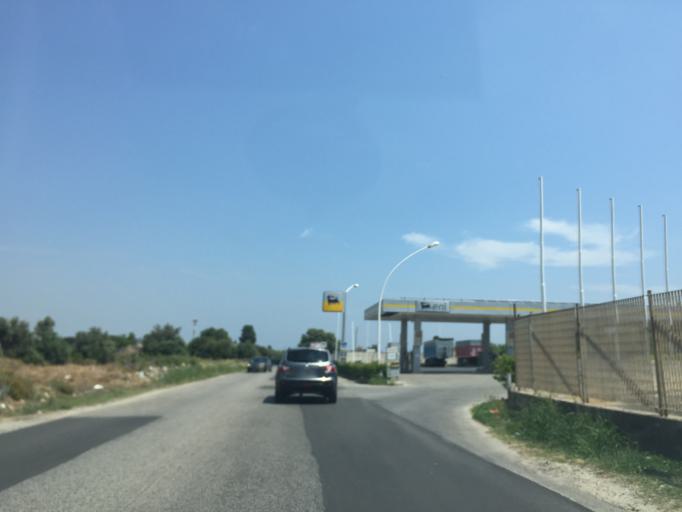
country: IT
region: Sicily
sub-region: Provincia di Siracusa
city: Avola
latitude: 36.9212
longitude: 15.1511
